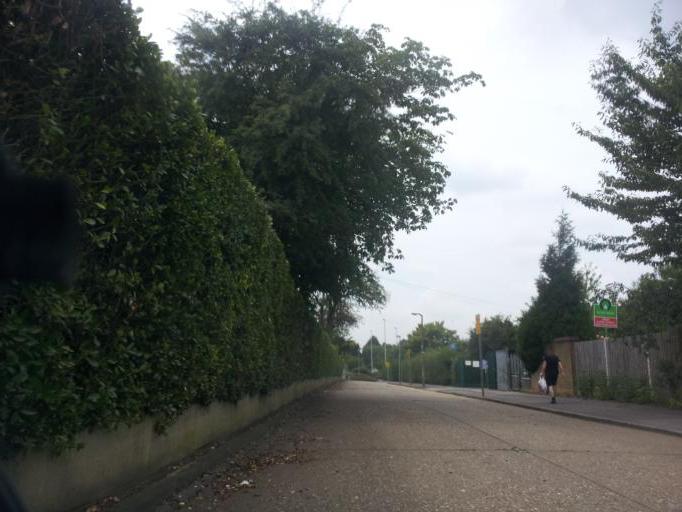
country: GB
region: England
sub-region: Kent
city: Gillingham
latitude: 51.3706
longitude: 0.5716
